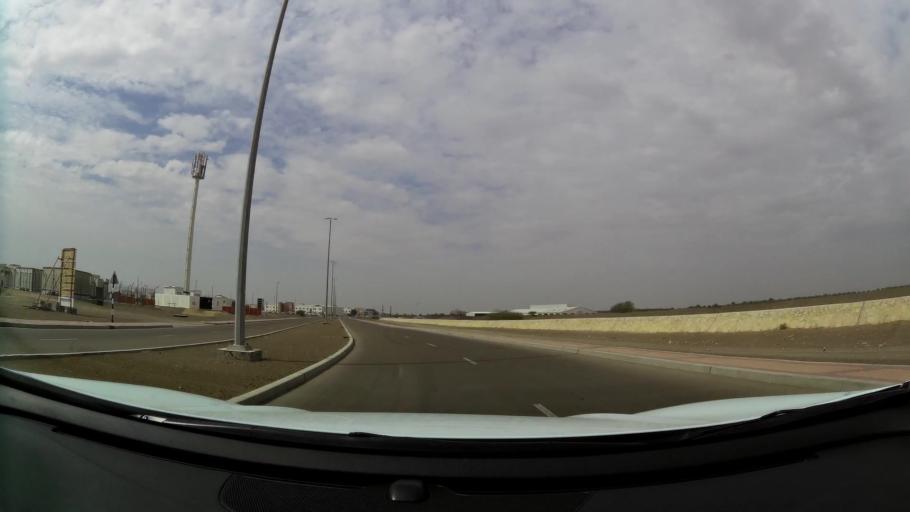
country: AE
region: Abu Dhabi
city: Al Ain
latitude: 24.1961
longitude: 55.8128
